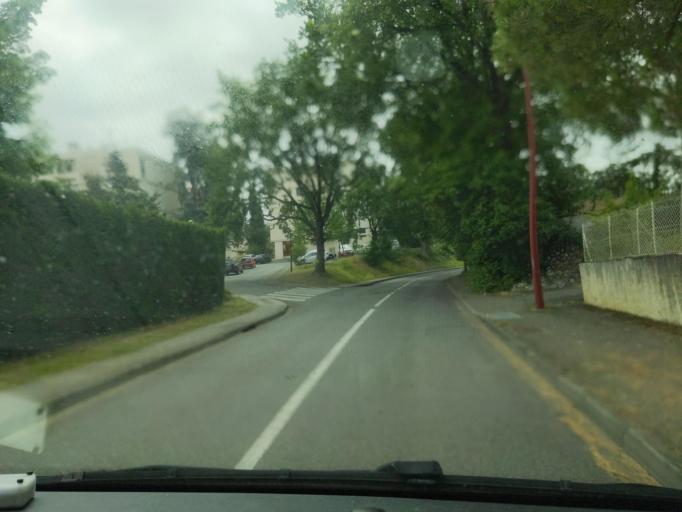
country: FR
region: Midi-Pyrenees
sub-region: Departement de la Haute-Garonne
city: Ramonville-Saint-Agne
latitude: 43.5375
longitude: 1.4778
